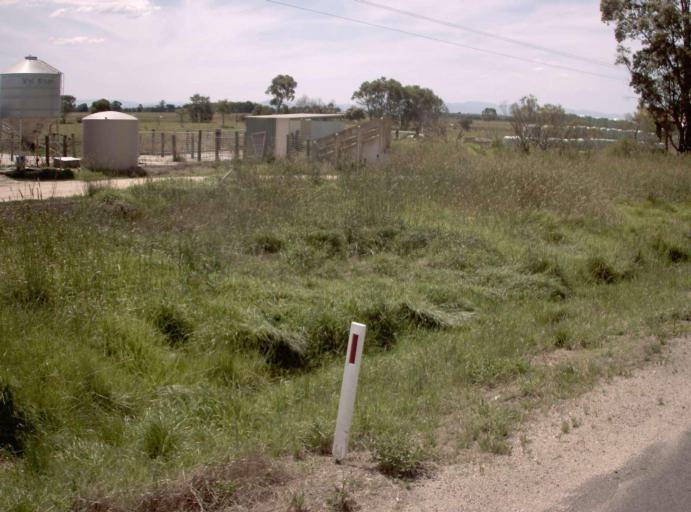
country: AU
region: Victoria
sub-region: Wellington
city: Sale
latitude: -38.0739
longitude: 147.0728
